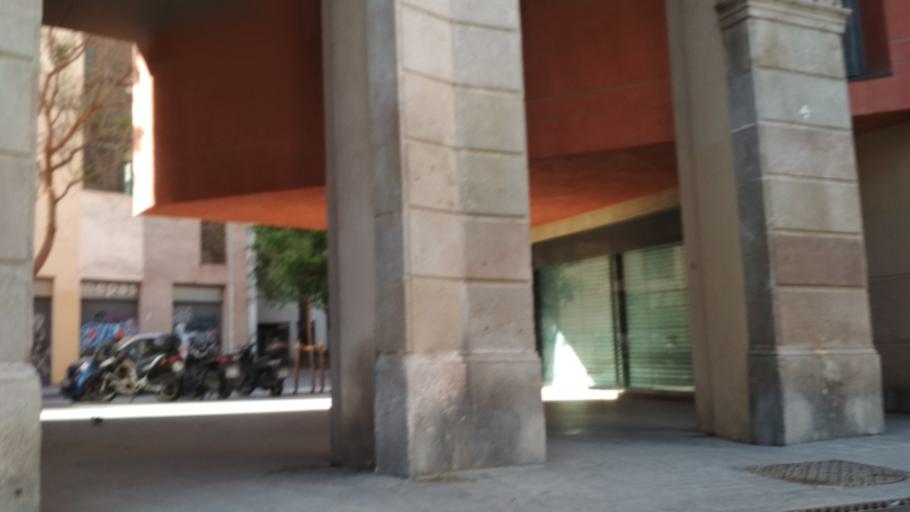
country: ES
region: Catalonia
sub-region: Provincia de Barcelona
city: Ciutat Vella
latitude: 41.3872
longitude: 2.1786
